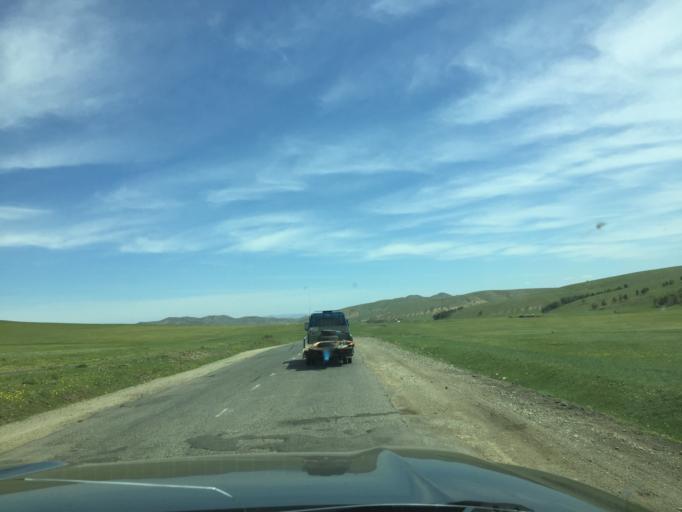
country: MN
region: Central Aimak
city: Javhlant
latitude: 48.6543
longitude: 106.1114
